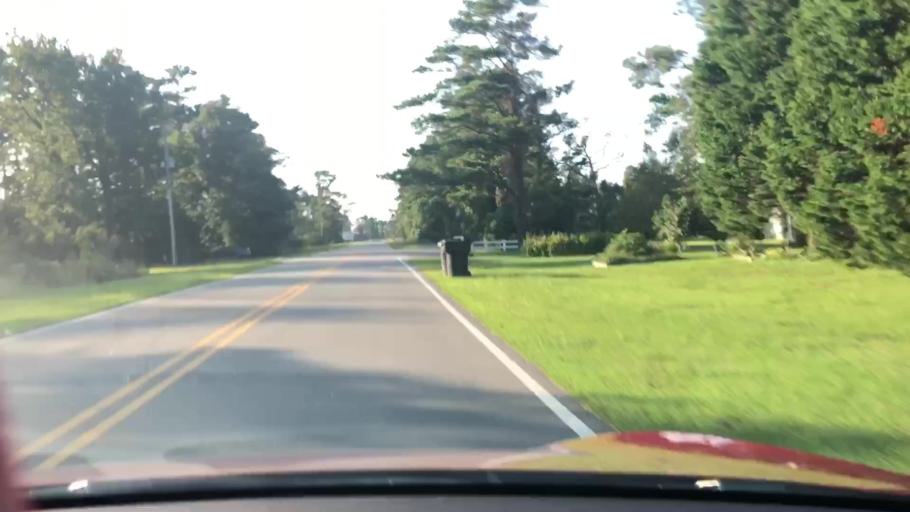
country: US
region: North Carolina
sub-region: Dare County
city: Manteo
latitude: 35.9001
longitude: -75.7709
